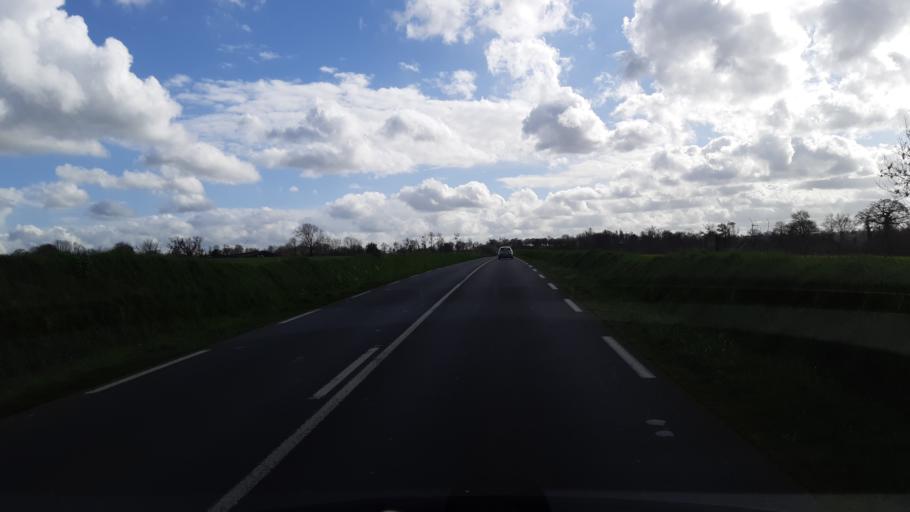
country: FR
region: Lower Normandy
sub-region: Departement de la Manche
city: Agneaux
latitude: 49.0407
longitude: -1.1308
